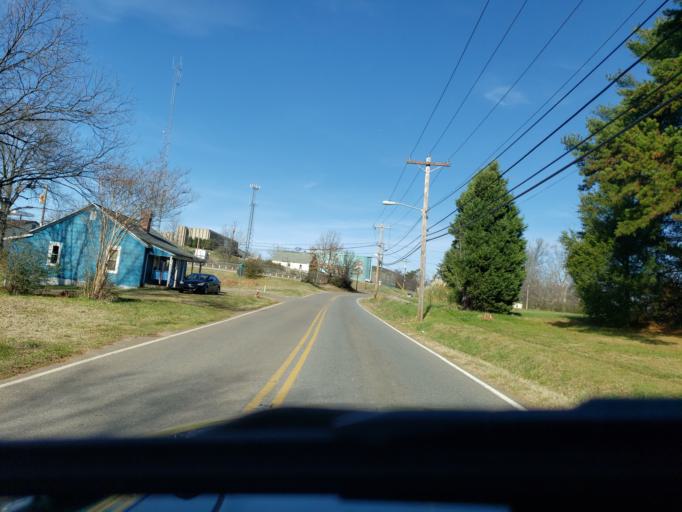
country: US
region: North Carolina
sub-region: Cleveland County
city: Kings Mountain
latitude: 35.2567
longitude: -81.3370
